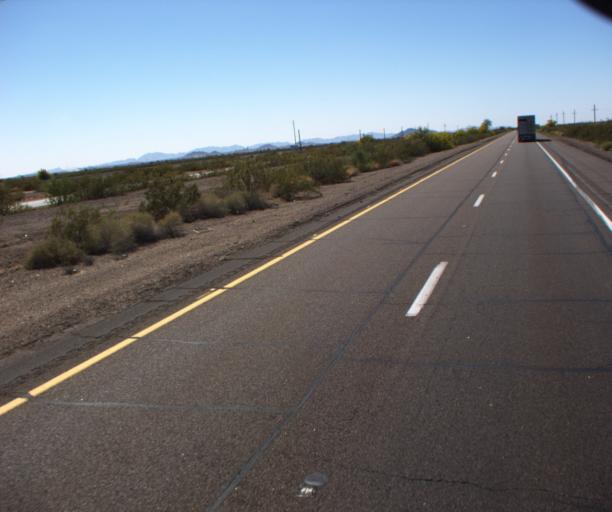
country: US
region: Arizona
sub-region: Maricopa County
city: Gila Bend
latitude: 32.8395
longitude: -113.3284
